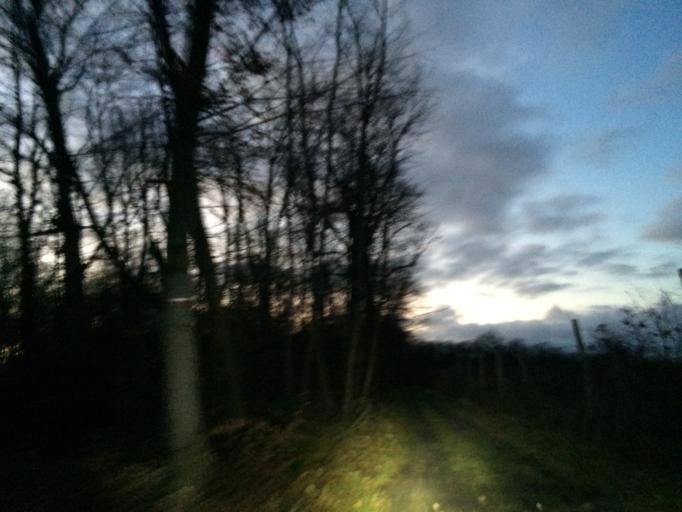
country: FR
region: Picardie
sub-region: Departement de l'Oise
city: Coye-la-Foret
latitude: 49.1487
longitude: 2.4865
